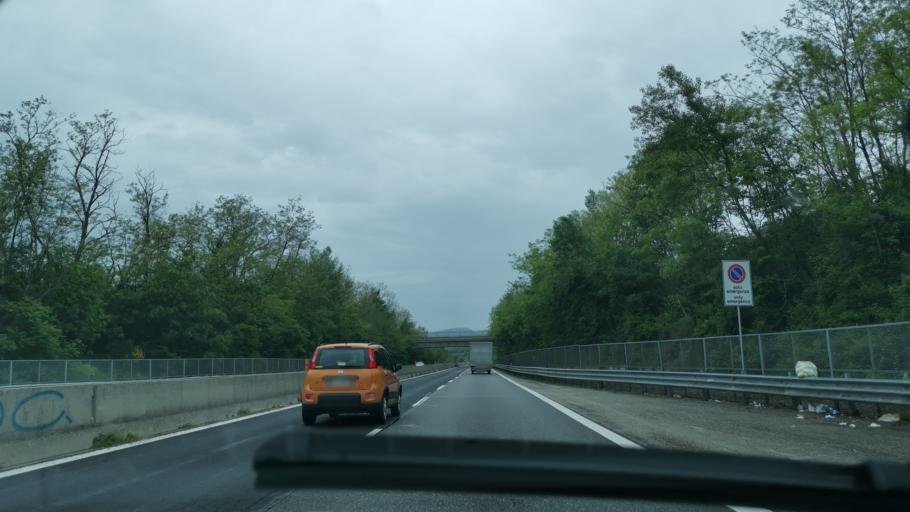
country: IT
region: Veneto
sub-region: Provincia di Verona
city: Calmasino
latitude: 45.5031
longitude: 10.7683
